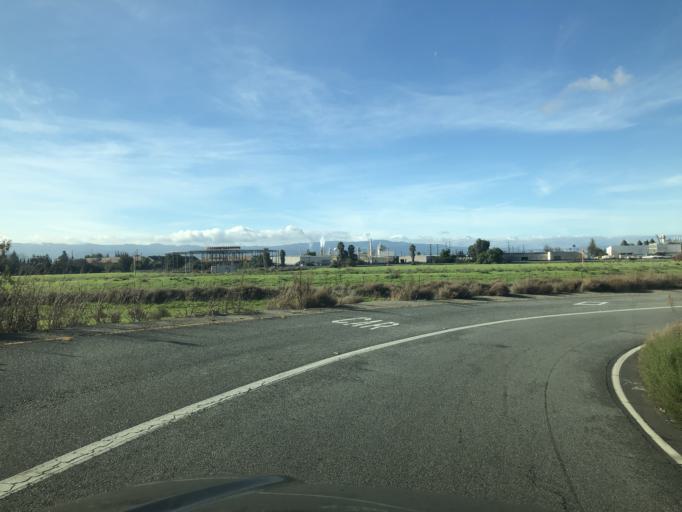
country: US
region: California
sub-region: Santa Clara County
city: Santa Clara
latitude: 37.3760
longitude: -121.9425
